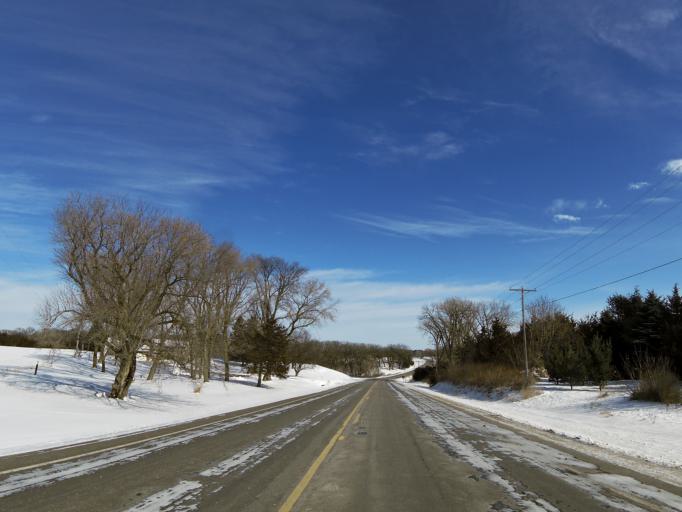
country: US
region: Wisconsin
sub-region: Pierce County
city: Prescott
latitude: 44.8099
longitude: -92.7477
